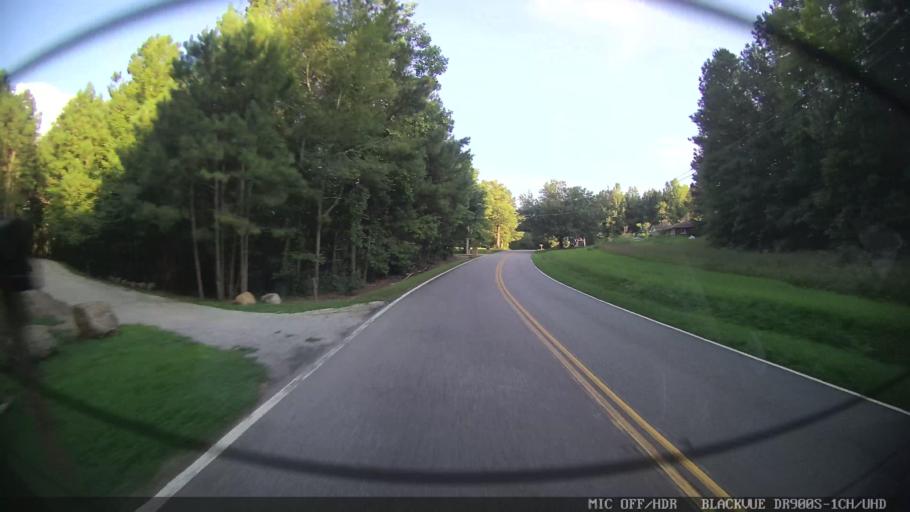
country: US
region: Georgia
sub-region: Bartow County
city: Emerson
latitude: 34.2119
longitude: -84.6938
